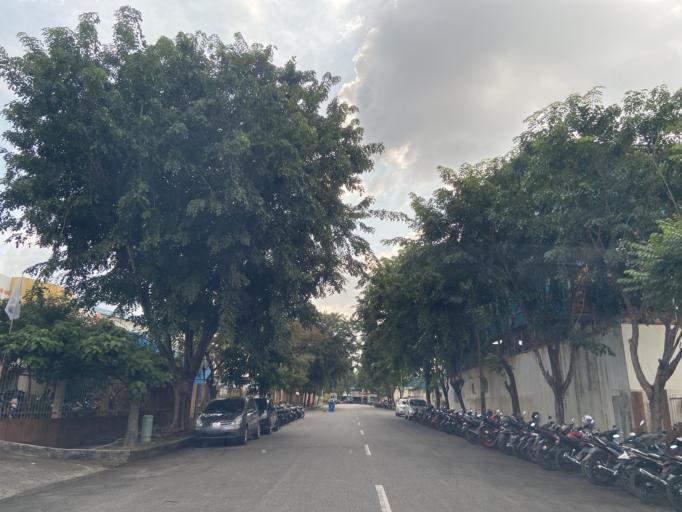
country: SG
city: Singapore
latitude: 1.1063
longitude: 104.0703
